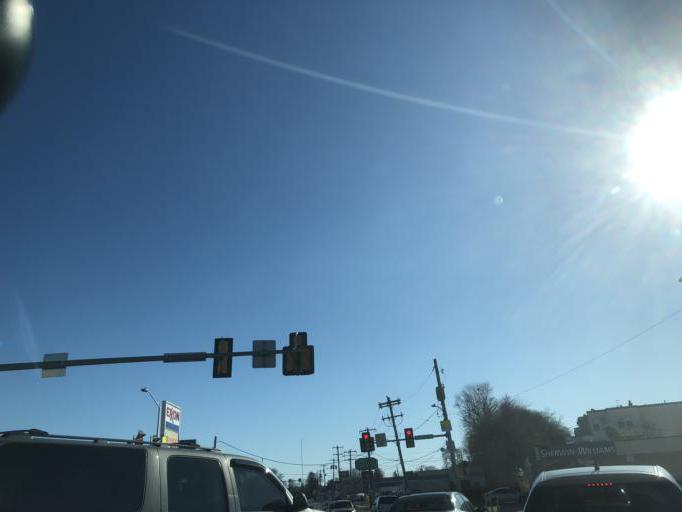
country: US
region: Pennsylvania
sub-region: Delaware County
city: East Lansdowne
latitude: 39.9540
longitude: -75.2587
